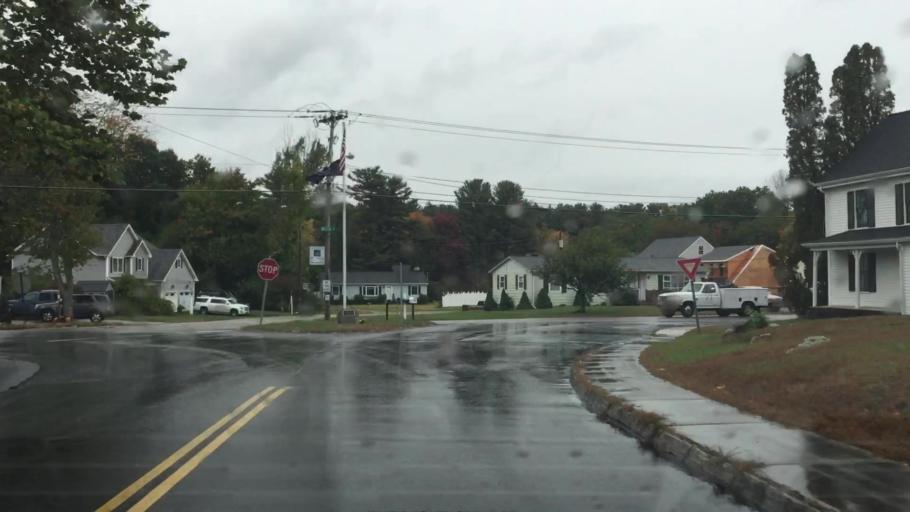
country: US
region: New Hampshire
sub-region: Rockingham County
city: Seabrook
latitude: 42.8757
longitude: -70.8561
